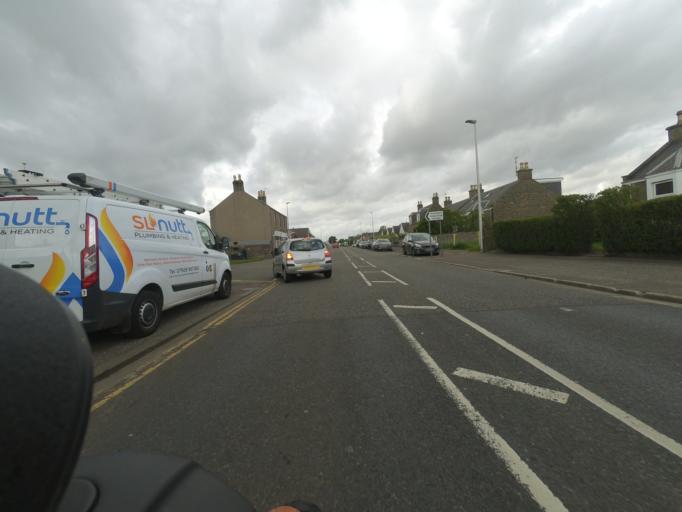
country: GB
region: Scotland
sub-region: Angus
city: Carnoustie
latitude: 56.5003
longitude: -2.7297
